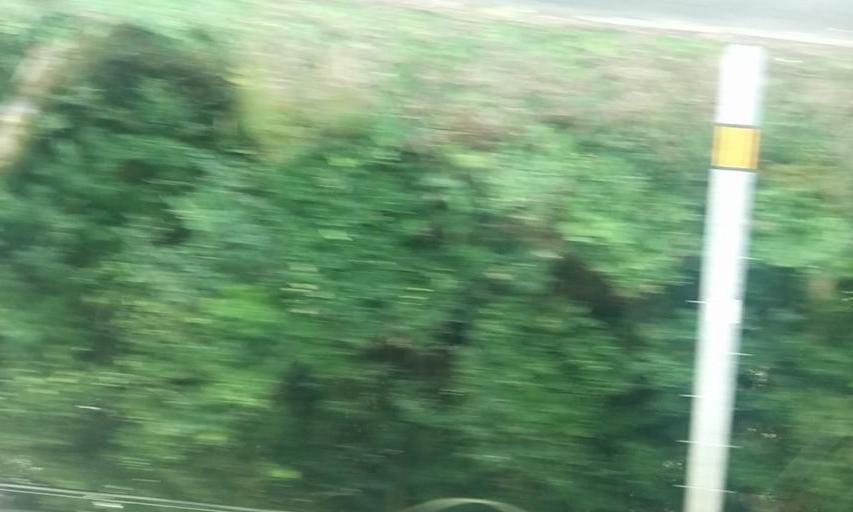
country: JP
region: Kyoto
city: Fukuchiyama
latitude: 35.3730
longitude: 135.1376
